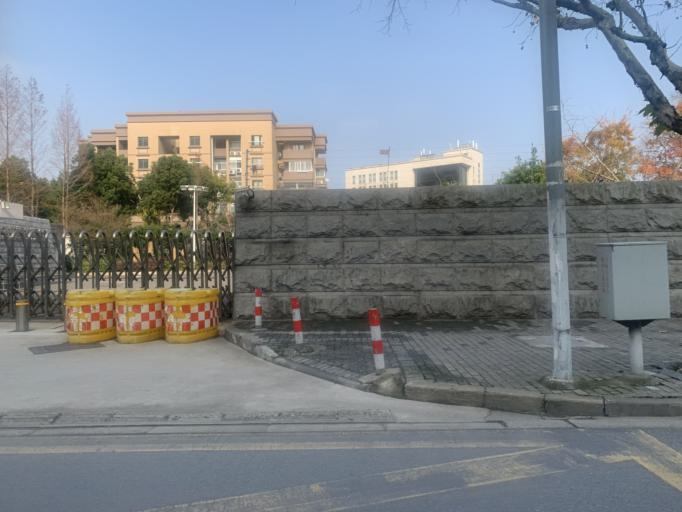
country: CN
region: Shanghai Shi
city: Huamu
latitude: 31.1828
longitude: 121.5214
